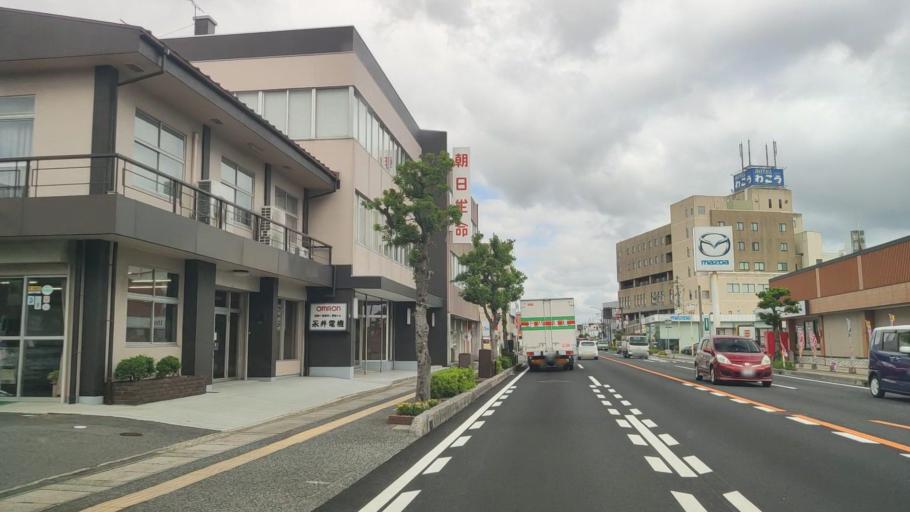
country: JP
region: Tottori
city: Yonago
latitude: 35.4380
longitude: 133.3429
